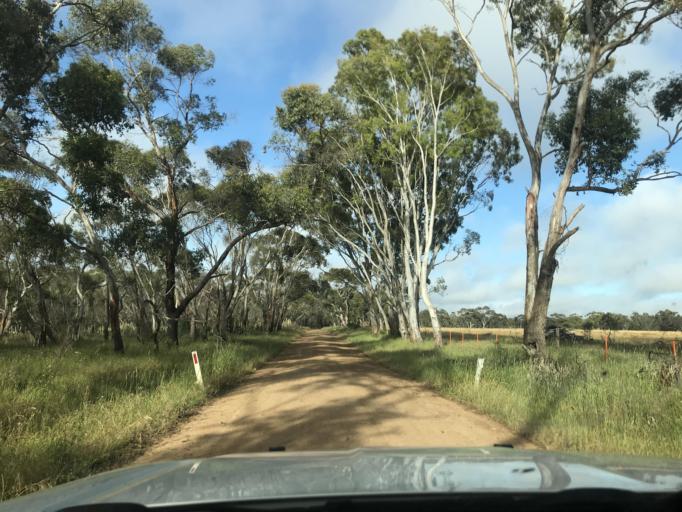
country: AU
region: South Australia
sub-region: Wattle Range
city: Penola
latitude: -37.1809
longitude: 141.1801
